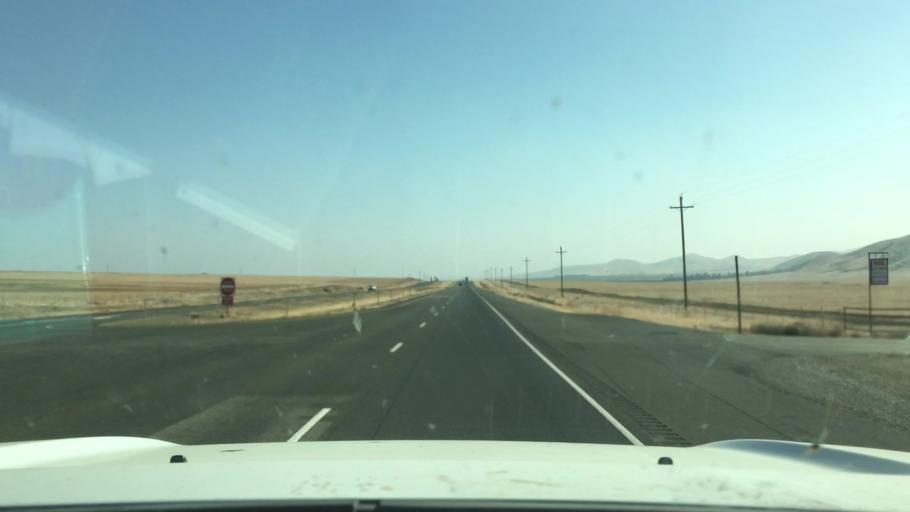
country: US
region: California
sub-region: San Luis Obispo County
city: Shandon
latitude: 35.7003
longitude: -120.1435
